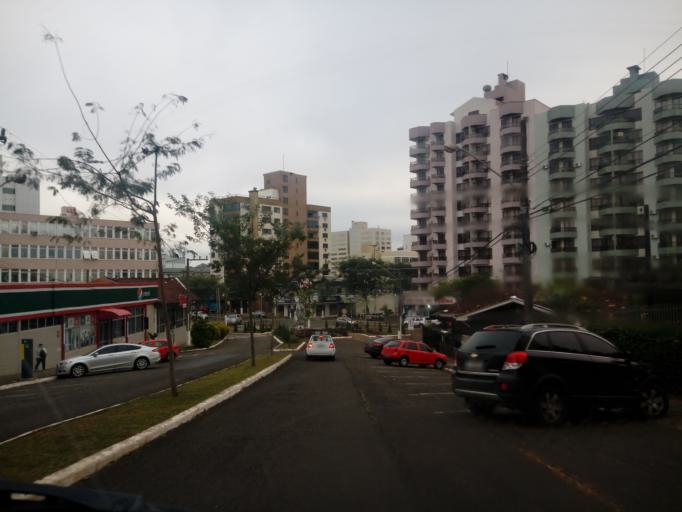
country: BR
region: Santa Catarina
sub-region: Chapeco
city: Chapeco
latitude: -27.1038
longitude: -52.6159
